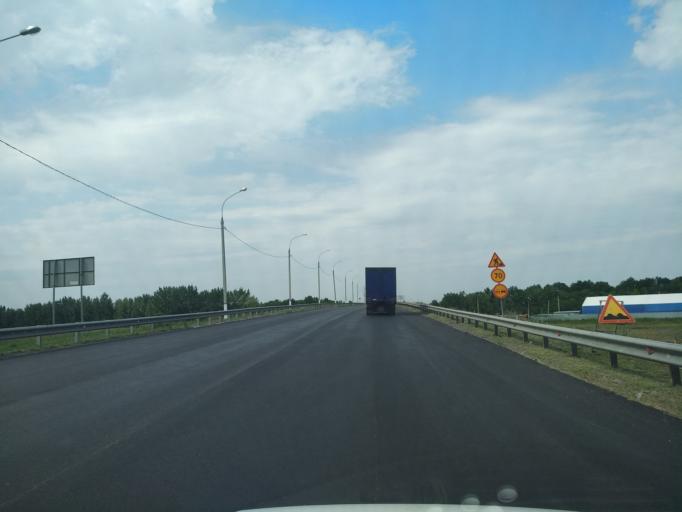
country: RU
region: Voronezj
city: Pereleshino
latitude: 51.7638
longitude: 40.1300
